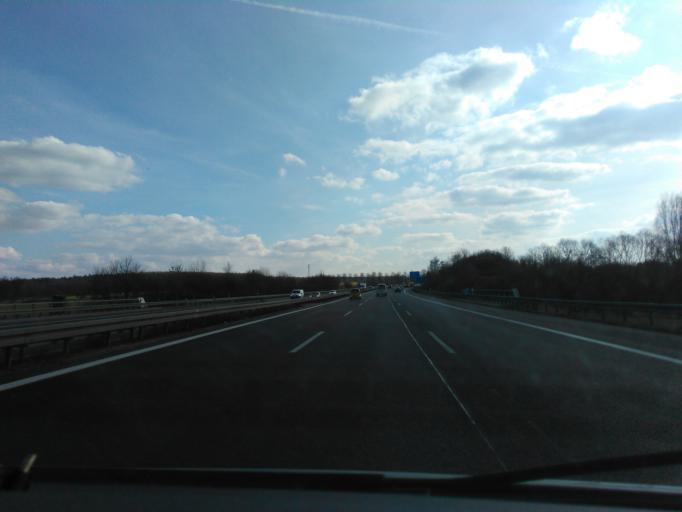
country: DE
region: Brandenburg
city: Schulzendorf
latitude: 52.3508
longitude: 13.5531
